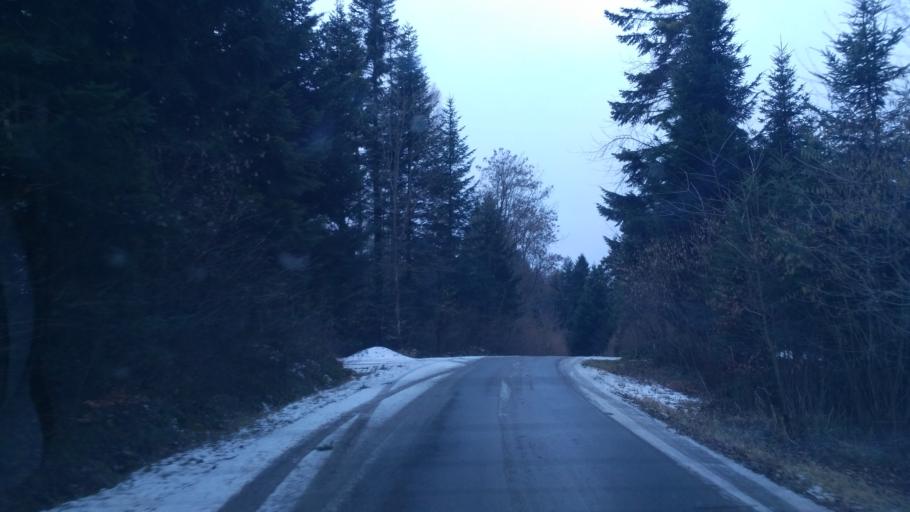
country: PL
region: Subcarpathian Voivodeship
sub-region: Powiat rzeszowski
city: Hyzne
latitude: 49.8954
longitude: 22.1553
